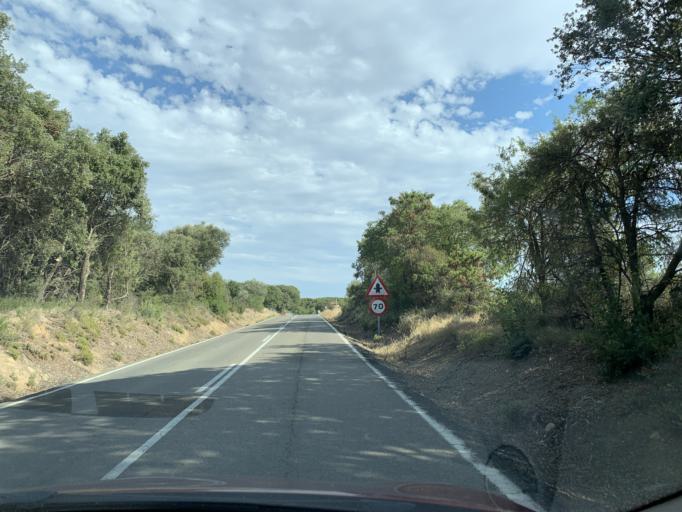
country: ES
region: Aragon
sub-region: Provincia de Zaragoza
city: Santa Eulalia de Gallego
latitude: 42.3071
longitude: -0.7464
